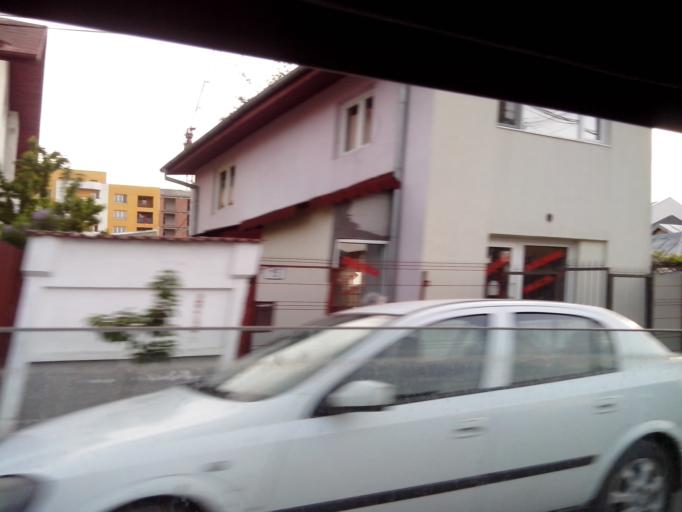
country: RO
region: Ilfov
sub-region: Comuna Chiajna
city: Rosu
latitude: 44.4443
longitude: 26.0344
